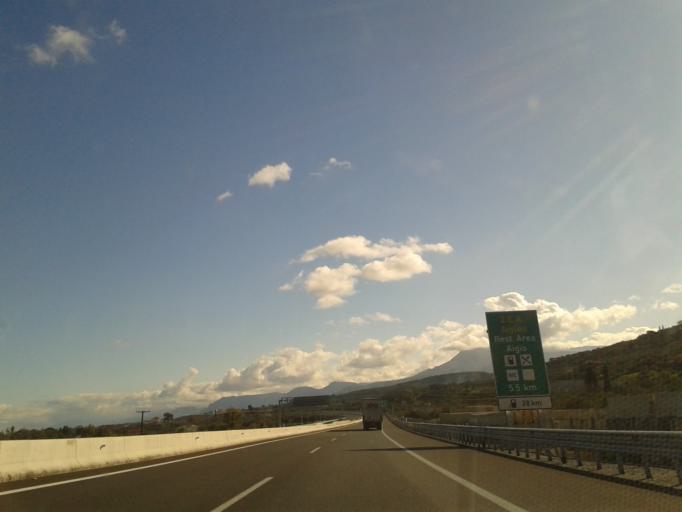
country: GR
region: West Greece
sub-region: Nomos Achaias
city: Selianitika
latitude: 38.2752
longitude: 22.0391
